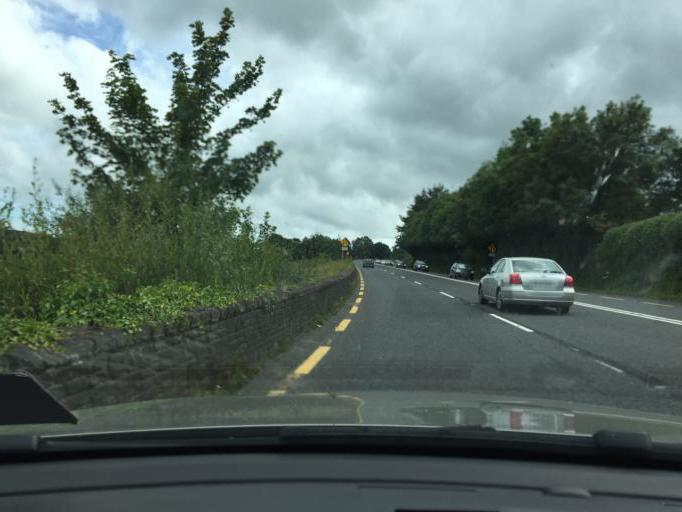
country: IE
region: Munster
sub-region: Waterford
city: Dungarvan
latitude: 52.1486
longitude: -7.5396
